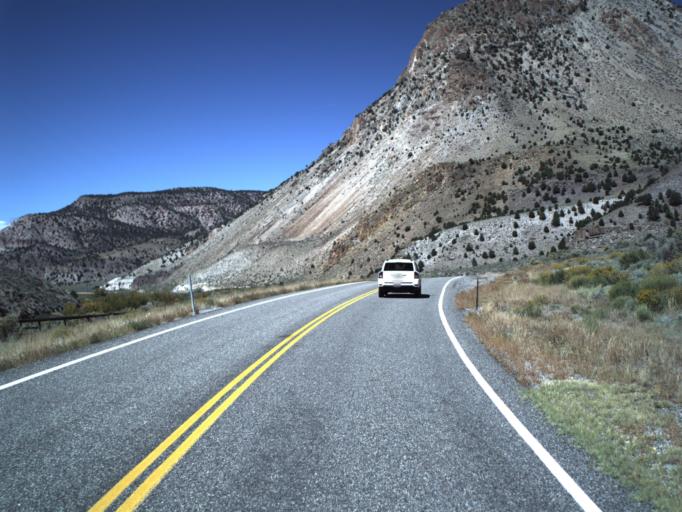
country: US
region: Utah
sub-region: Piute County
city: Junction
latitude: 38.1792
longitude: -112.0785
